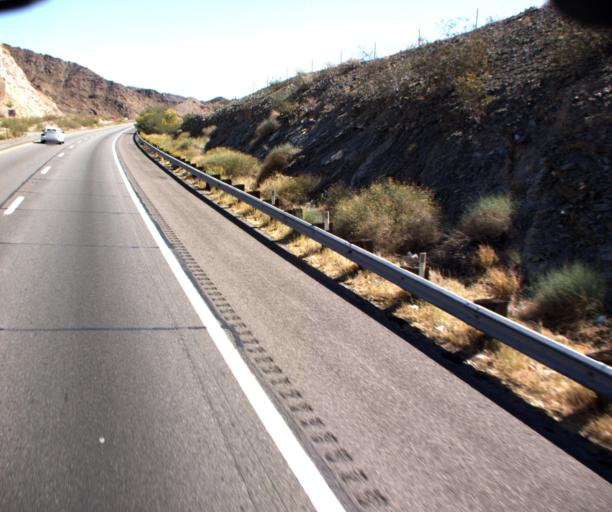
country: US
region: Arizona
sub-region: La Paz County
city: Ehrenberg
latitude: 33.6437
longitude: -114.3814
